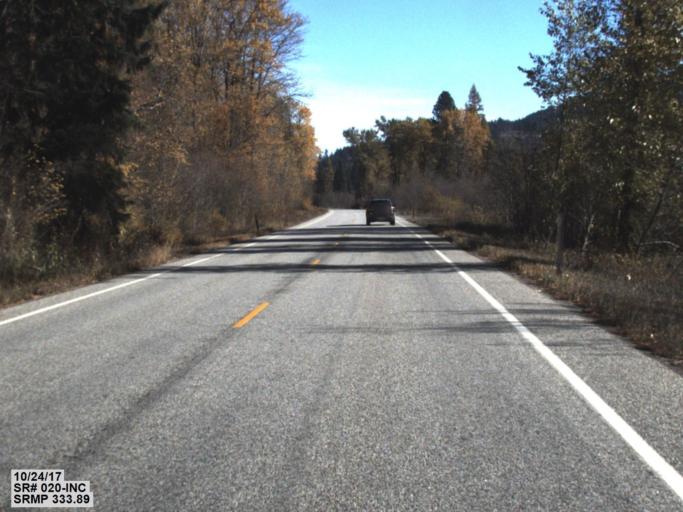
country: US
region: Washington
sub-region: Stevens County
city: Kettle Falls
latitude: 48.5791
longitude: -118.2520
